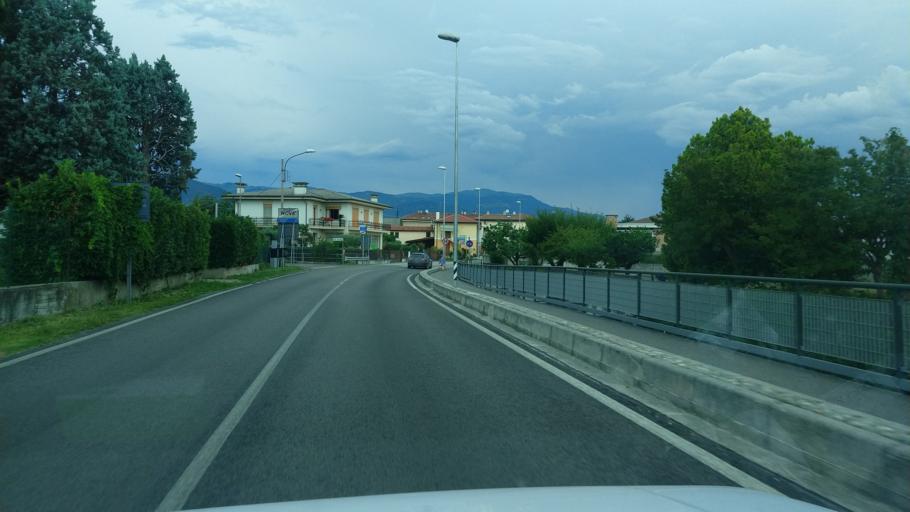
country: IT
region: Veneto
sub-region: Provincia di Vicenza
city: Nove
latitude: 45.7342
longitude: 11.6872
